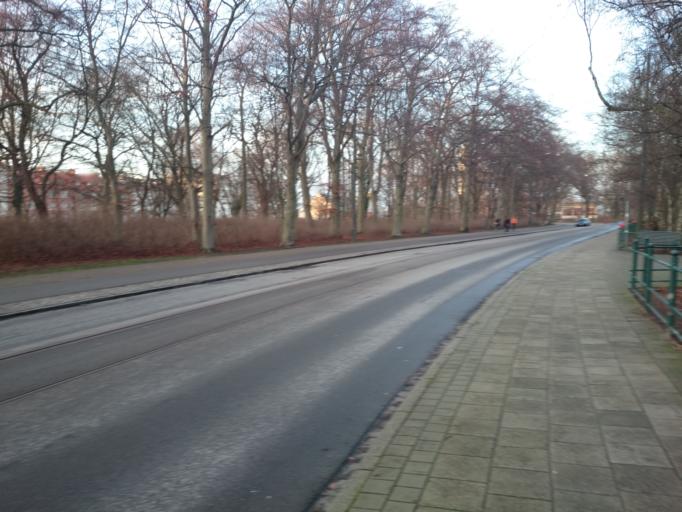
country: SE
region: Skane
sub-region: Malmo
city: Malmoe
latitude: 55.6014
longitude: 12.9844
